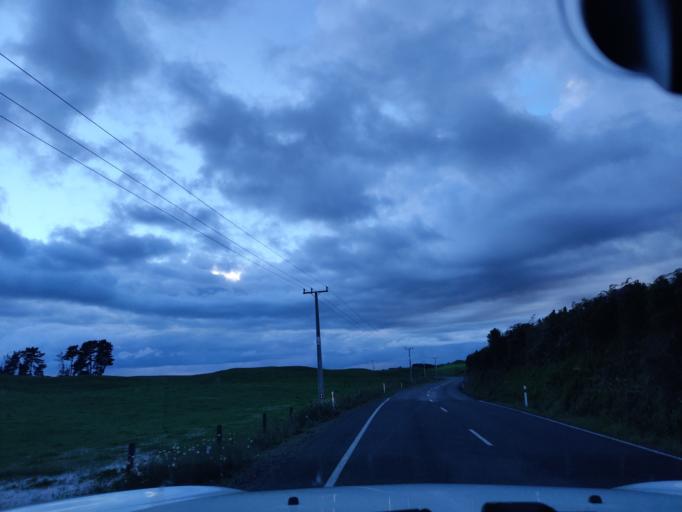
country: NZ
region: Waikato
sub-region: South Waikato District
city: Tokoroa
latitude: -38.1673
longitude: 175.7682
